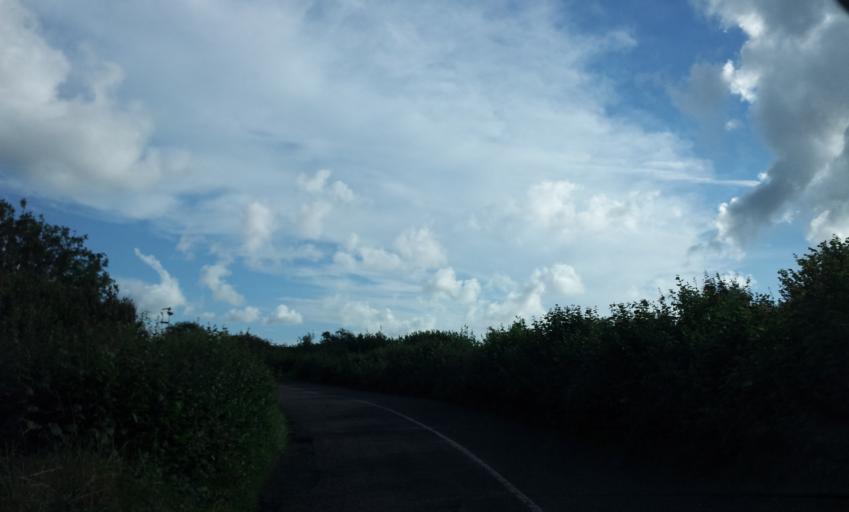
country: IE
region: Connaught
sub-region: County Galway
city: Bearna
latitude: 53.0535
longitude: -9.1468
